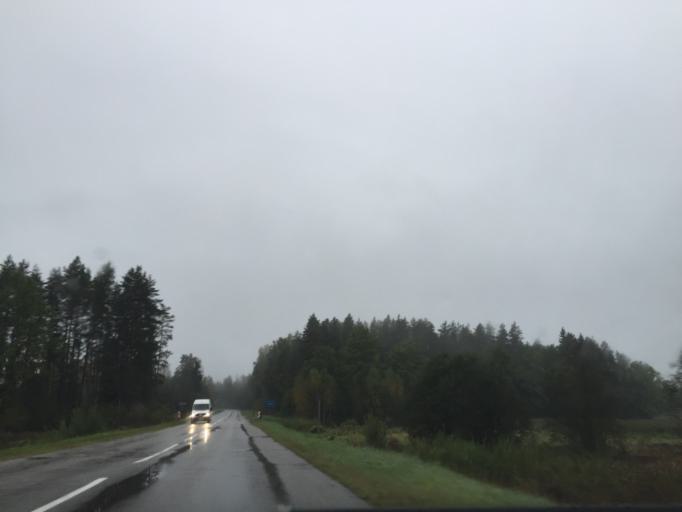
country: LV
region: Incukalns
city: Incukalns
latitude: 57.0298
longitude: 24.6827
